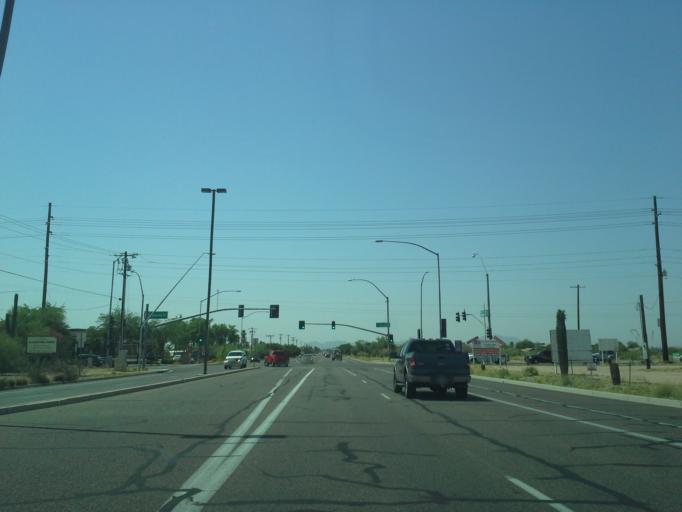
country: US
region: Arizona
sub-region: Pinal County
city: Apache Junction
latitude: 33.4233
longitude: -111.6327
